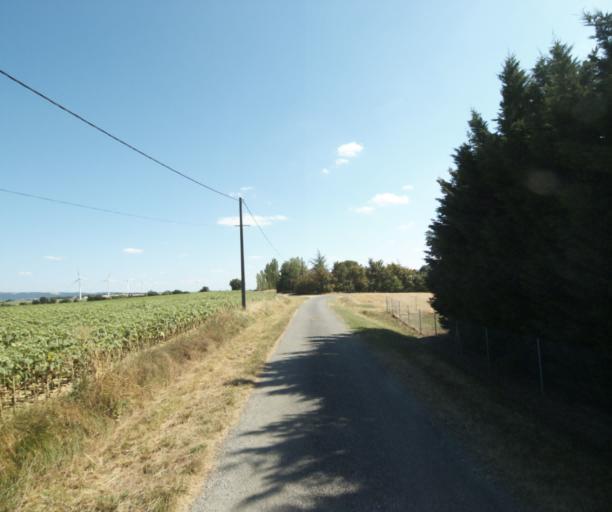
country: FR
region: Midi-Pyrenees
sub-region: Departement de la Haute-Garonne
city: Saint-Felix-Lauragais
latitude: 43.4796
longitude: 1.9083
